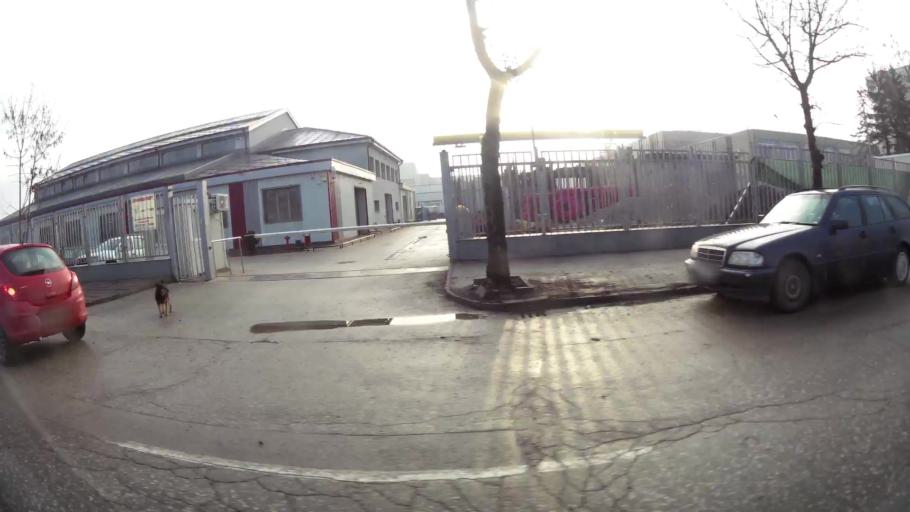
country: BG
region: Sofia-Capital
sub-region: Stolichna Obshtina
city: Sofia
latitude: 42.7315
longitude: 23.3211
